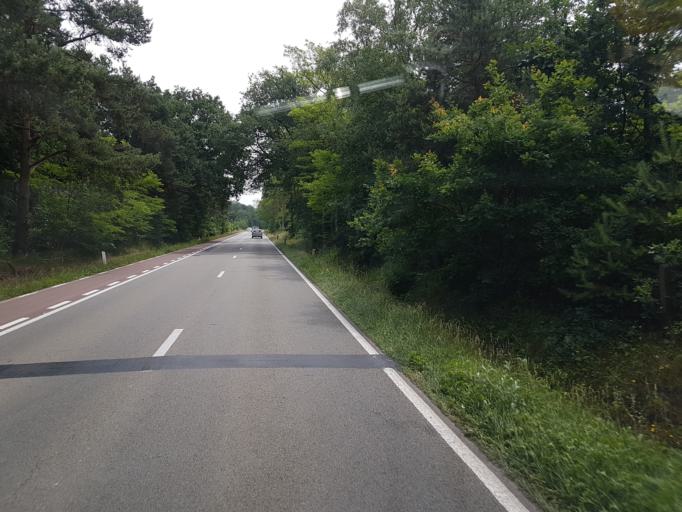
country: BE
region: Flanders
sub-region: Provincie Antwerpen
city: Oostmalle
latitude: 51.2755
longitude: 4.7693
